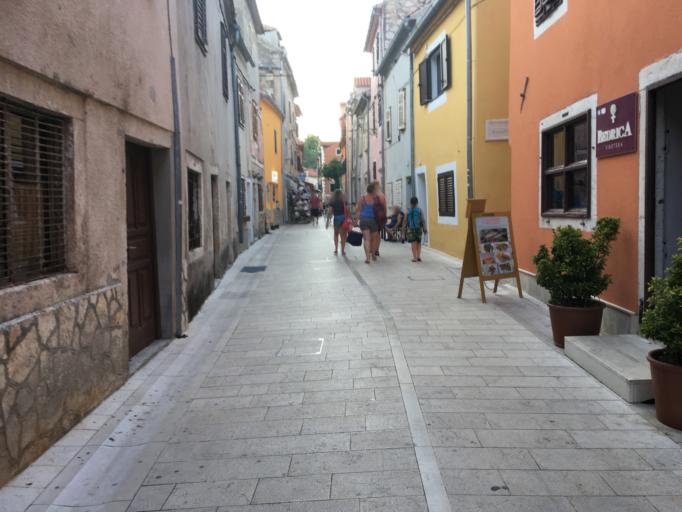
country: HR
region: Sibensko-Kniniska
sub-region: Grad Sibenik
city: Sibenik
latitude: 43.8187
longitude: 15.9228
